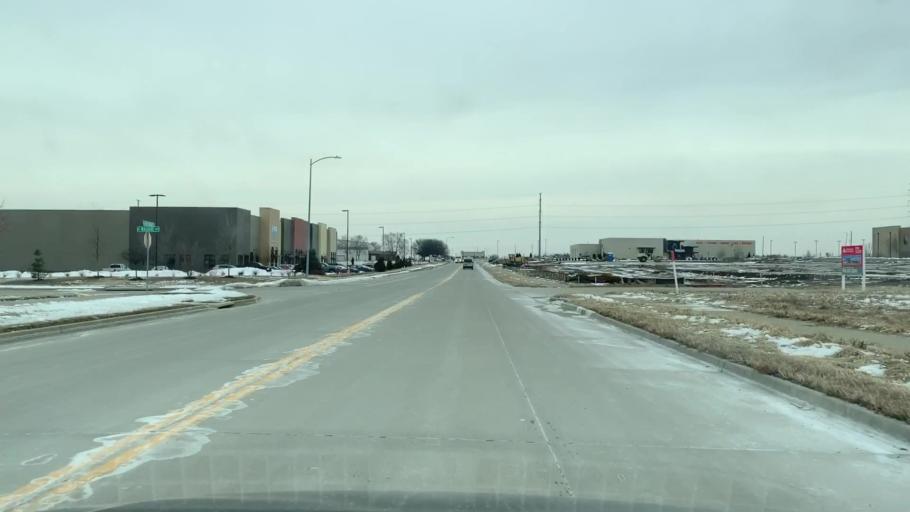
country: US
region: Missouri
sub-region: Jackson County
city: Lees Summit
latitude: 38.9620
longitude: -94.3616
